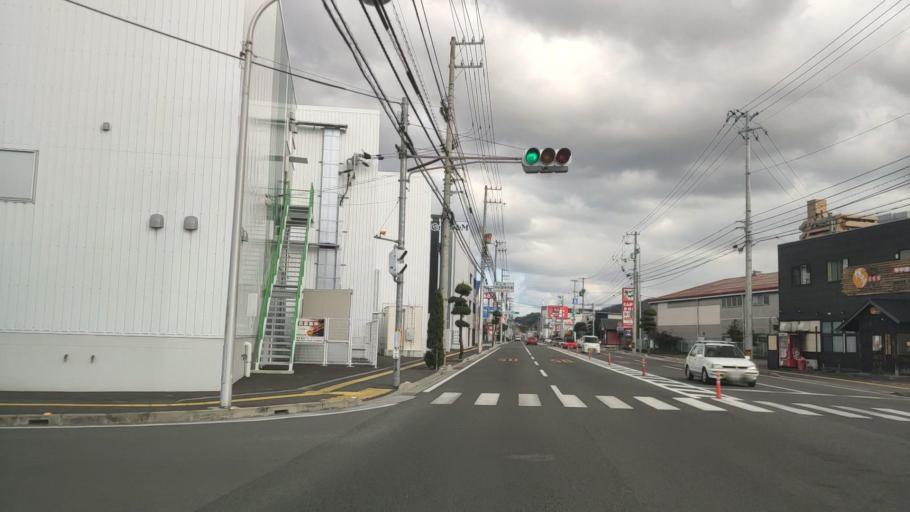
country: JP
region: Ehime
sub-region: Shikoku-chuo Shi
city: Matsuyama
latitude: 33.8609
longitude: 132.7494
